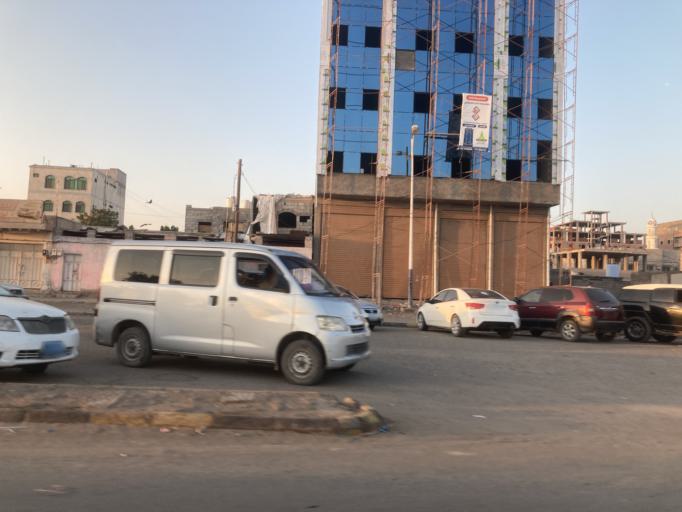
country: YE
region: Aden
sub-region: Al Mansura
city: Al Mansurah
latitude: 12.8564
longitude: 44.9935
